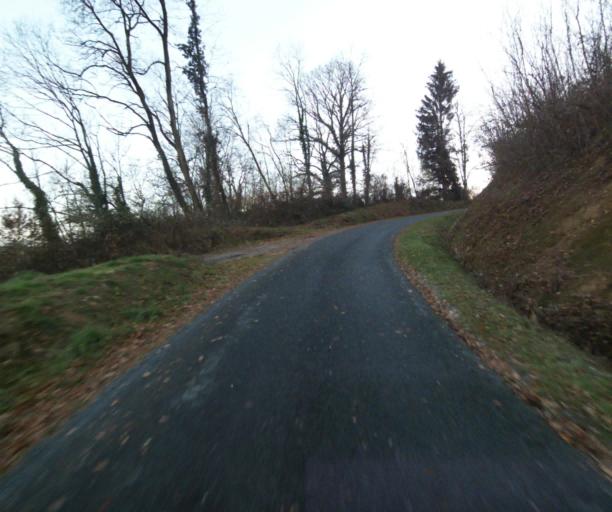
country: FR
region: Limousin
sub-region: Departement de la Correze
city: Laguenne
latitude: 45.2373
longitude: 1.7716
